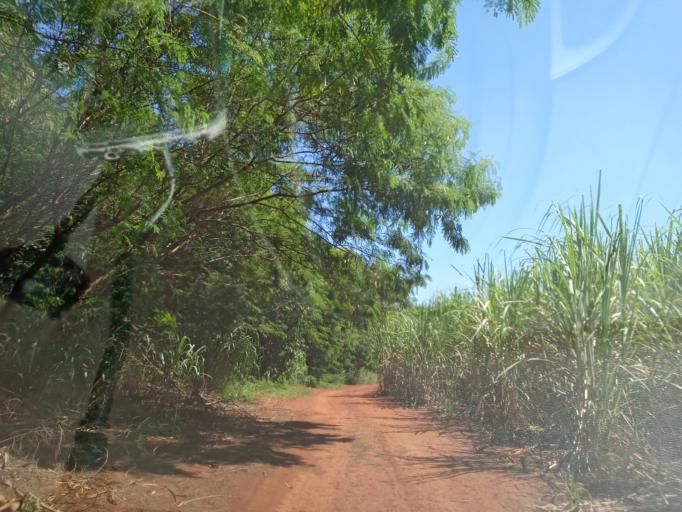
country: BR
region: Goias
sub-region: Itumbiara
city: Itumbiara
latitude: -18.4416
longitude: -49.1420
